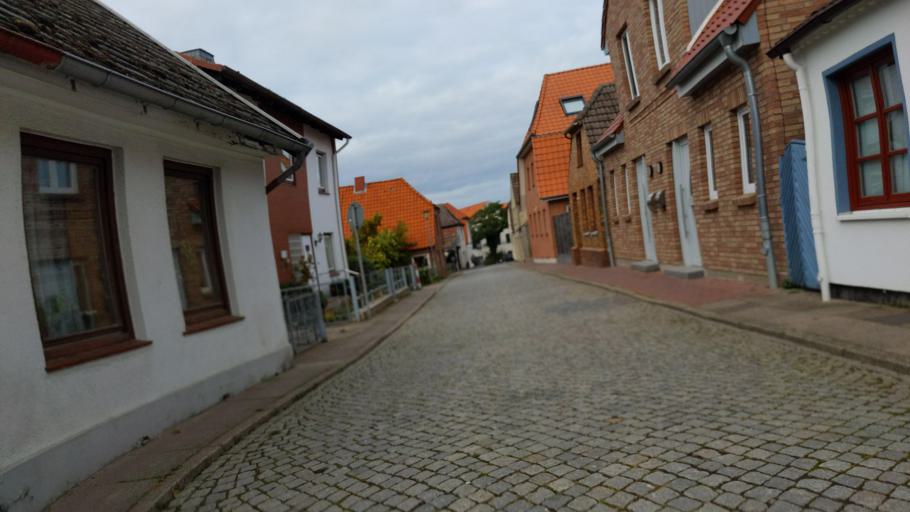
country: DE
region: Schleswig-Holstein
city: Neustadt in Holstein
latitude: 54.1086
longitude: 10.8175
